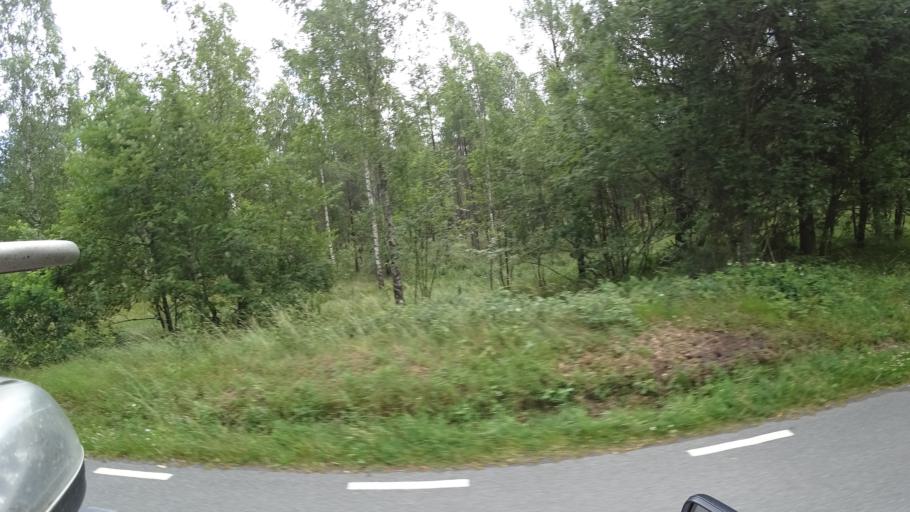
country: SE
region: Skane
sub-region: Kristianstads Kommun
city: Degeberga
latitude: 55.7182
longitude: 13.9908
